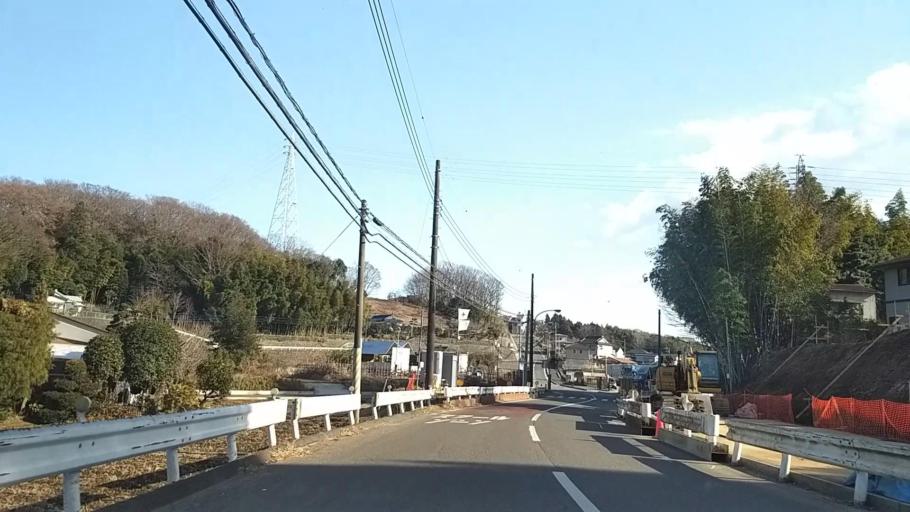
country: JP
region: Kanagawa
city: Atsugi
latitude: 35.4578
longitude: 139.3217
